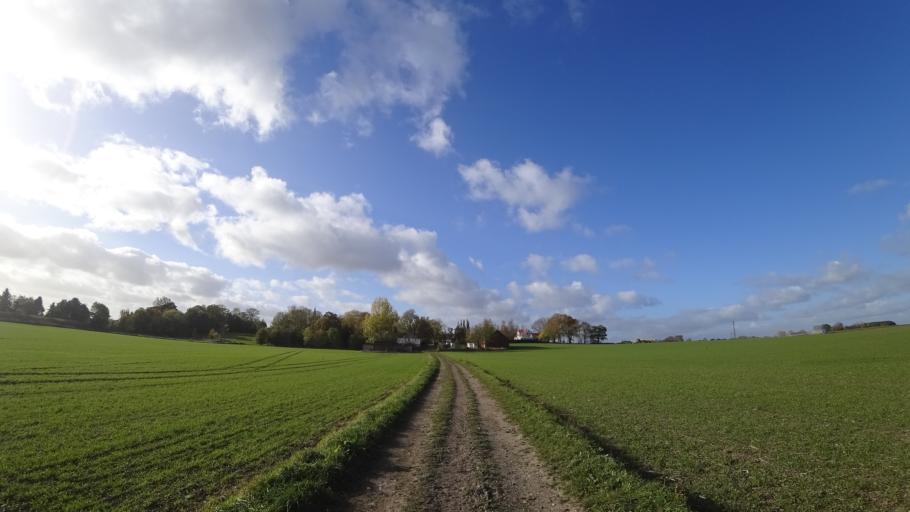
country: SE
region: Skane
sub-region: Staffanstorps Kommun
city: Hjaerup
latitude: 55.6290
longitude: 13.1501
